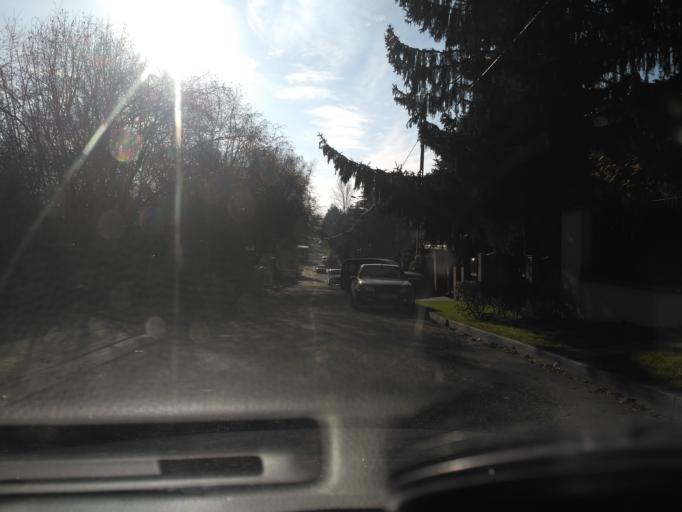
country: PL
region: Lublin Voivodeship
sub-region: Powiat lubelski
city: Lublin
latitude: 51.2643
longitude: 22.5393
